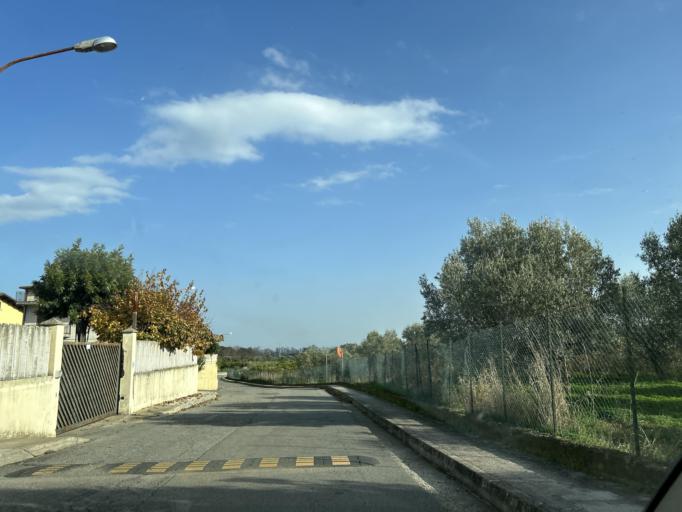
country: IT
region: Calabria
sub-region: Provincia di Catanzaro
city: Montepaone Lido
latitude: 38.7148
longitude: 16.5258
